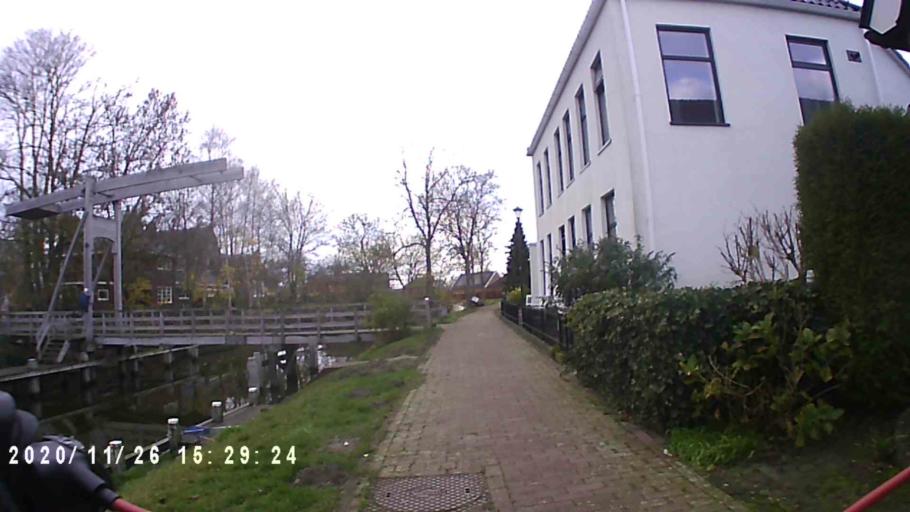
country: NL
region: Groningen
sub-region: Gemeente Appingedam
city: Appingedam
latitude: 53.3110
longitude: 6.7602
